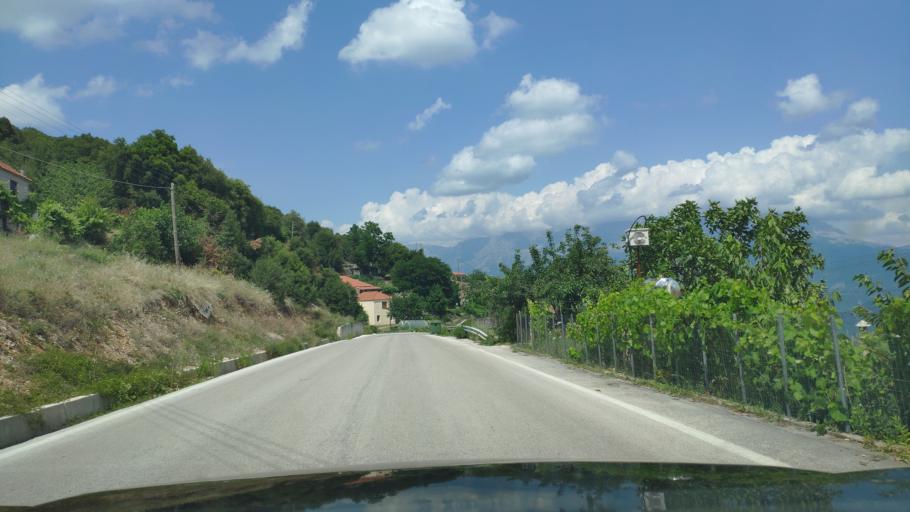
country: GR
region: Epirus
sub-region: Nomos Artas
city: Agios Dimitrios
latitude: 39.3316
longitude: 20.9996
